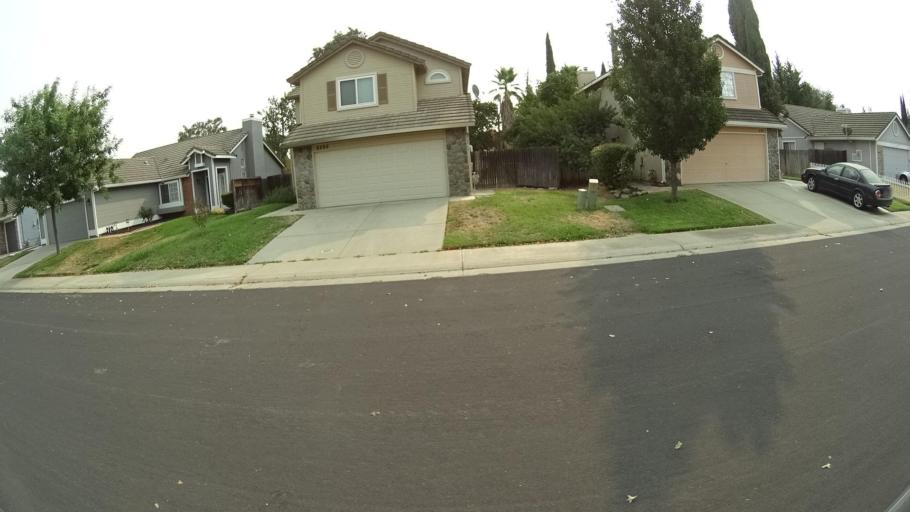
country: US
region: California
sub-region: Sacramento County
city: Laguna
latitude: 38.4178
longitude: -121.3984
